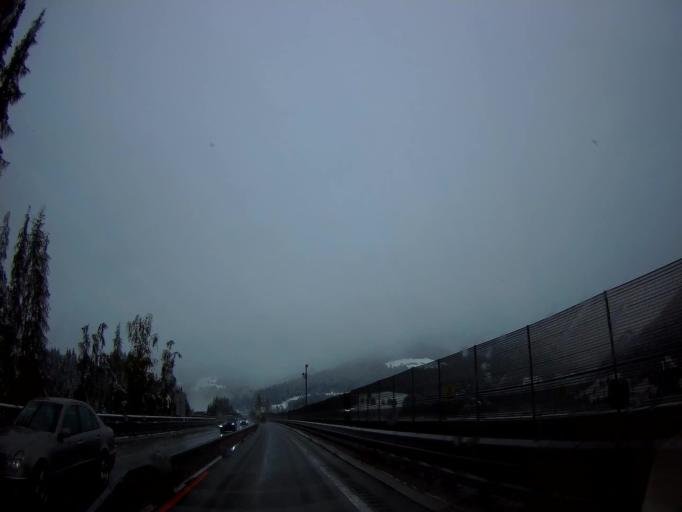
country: AT
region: Salzburg
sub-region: Politischer Bezirk Sankt Johann im Pongau
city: Huttau
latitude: 47.4179
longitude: 13.3143
